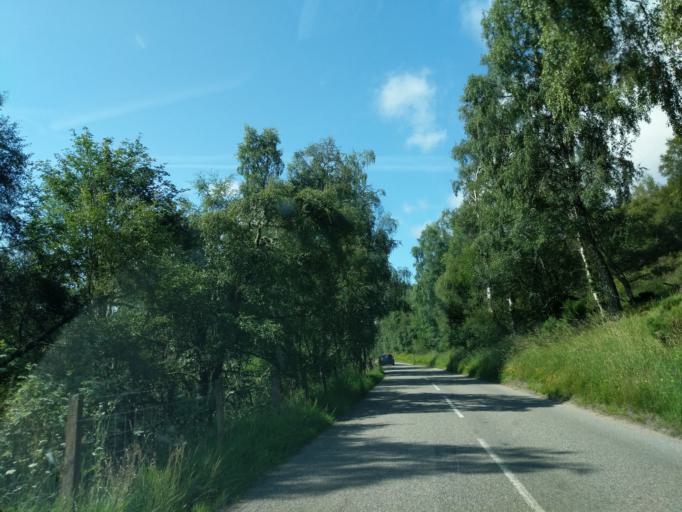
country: GB
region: Scotland
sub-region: Moray
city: Dufftown
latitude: 57.3700
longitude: -3.2559
